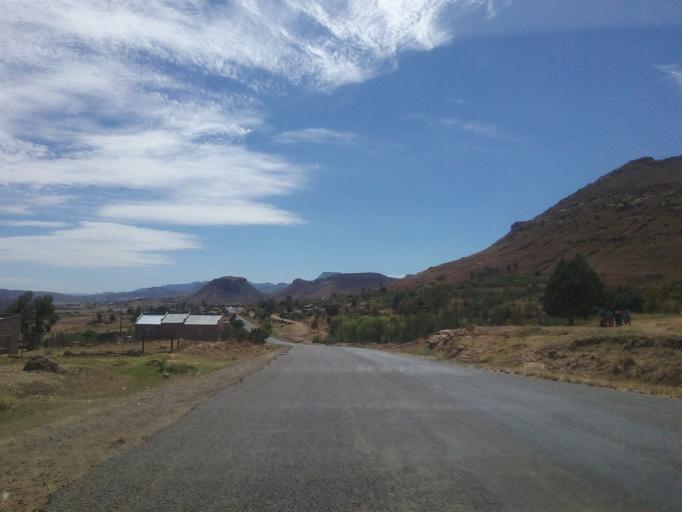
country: LS
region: Mohale's Hoek District
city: Mohale's Hoek
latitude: -30.1865
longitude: 27.4208
